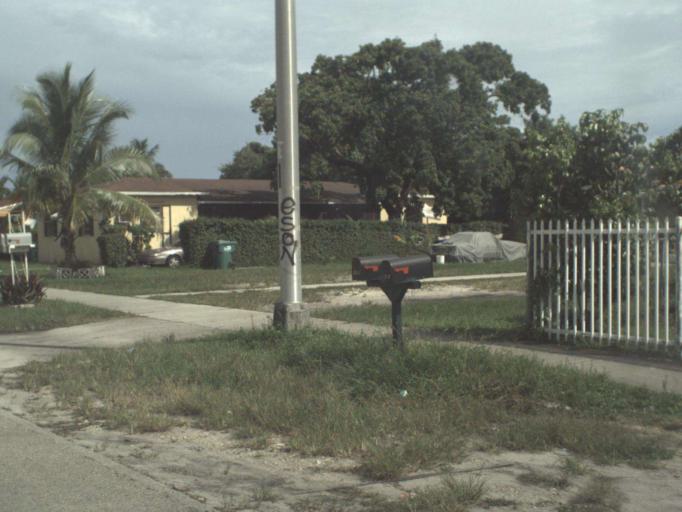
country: US
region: Florida
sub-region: Miami-Dade County
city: North Miami
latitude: 25.8841
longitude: -80.2013
